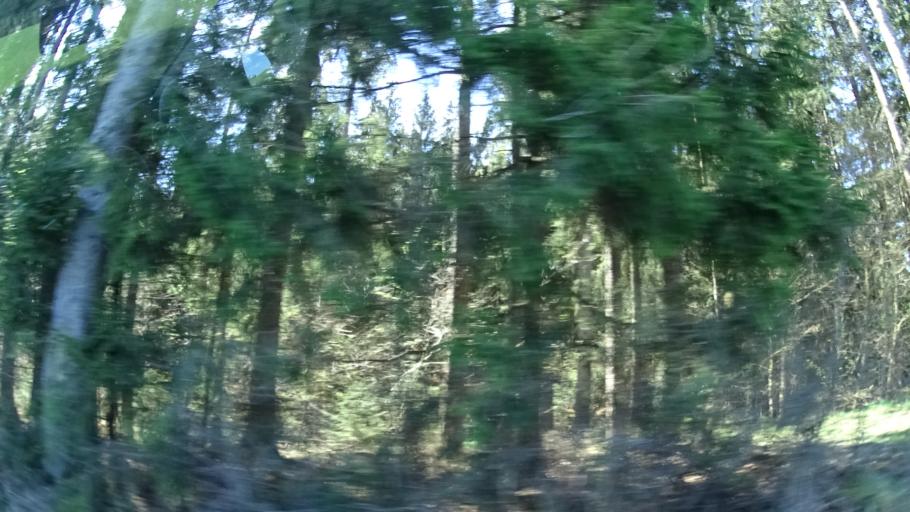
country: DE
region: Bavaria
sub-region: Upper Palatinate
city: Kastl
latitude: 49.3968
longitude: 11.6760
